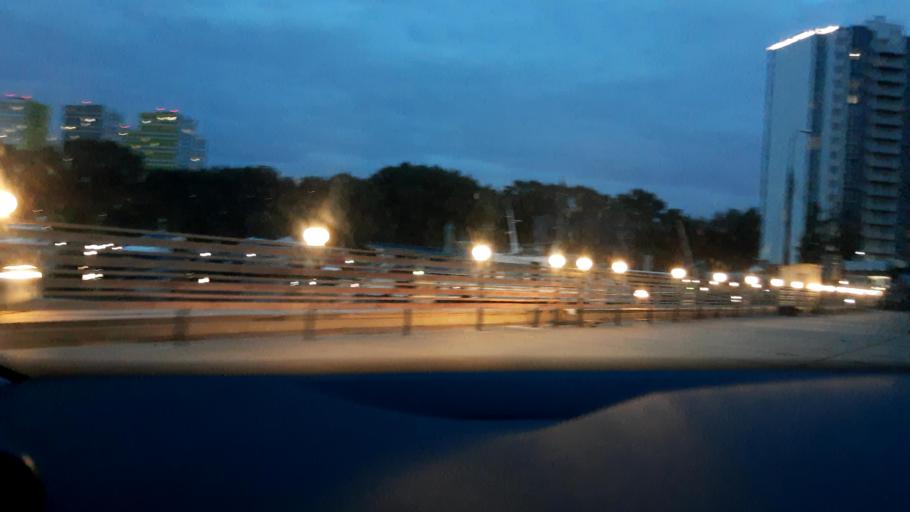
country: RU
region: Moskovskaya
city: Levoberezhnaya
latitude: 55.8981
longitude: 37.4644
